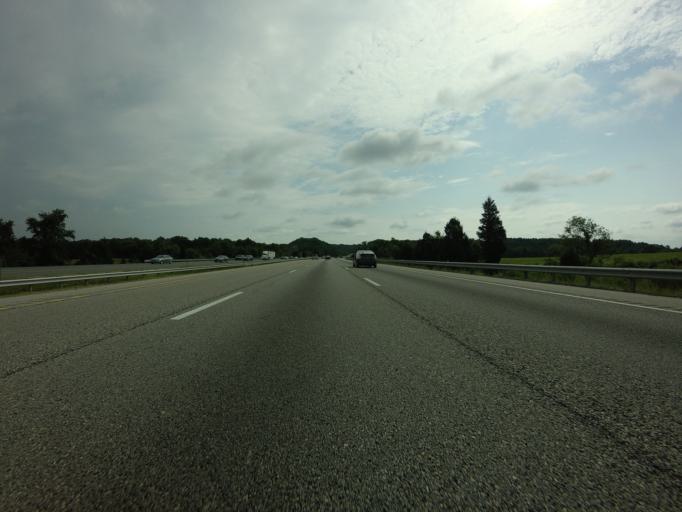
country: US
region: Maryland
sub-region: Cecil County
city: North East
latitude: 39.6419
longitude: -75.9370
